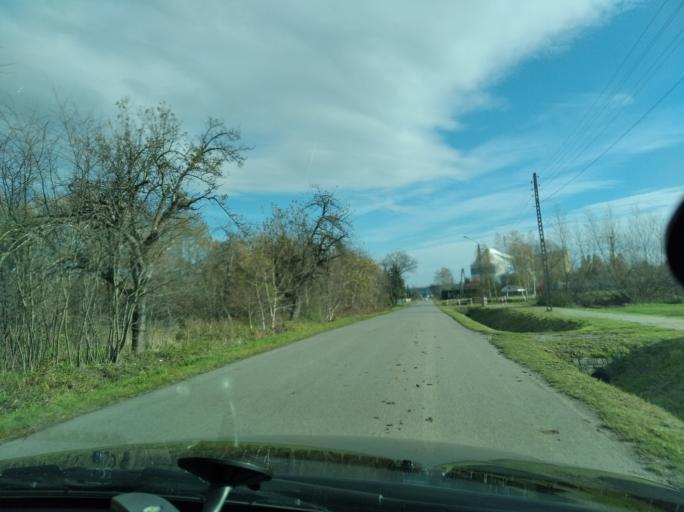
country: PL
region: Subcarpathian Voivodeship
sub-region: Powiat ropczycko-sedziszowski
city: Ostrow
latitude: 50.0861
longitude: 21.5831
